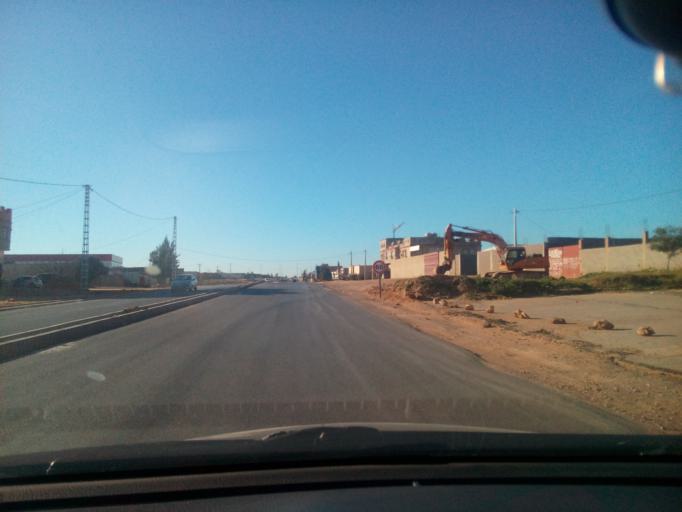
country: DZ
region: Mostaganem
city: Mostaganem
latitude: 35.9101
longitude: 0.1586
